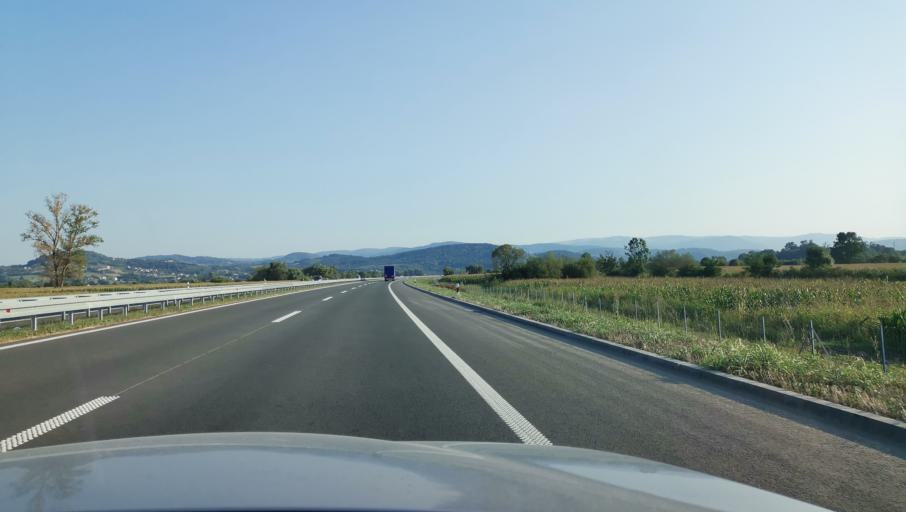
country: RS
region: Central Serbia
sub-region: Kolubarski Okrug
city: Ljig
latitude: 44.2615
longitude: 20.2709
